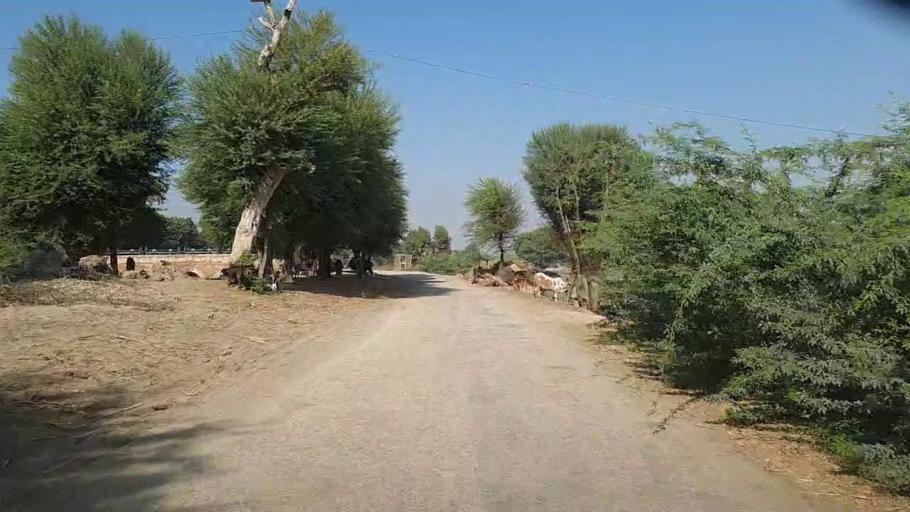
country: PK
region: Sindh
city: Bozdar
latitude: 27.1975
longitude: 68.6653
